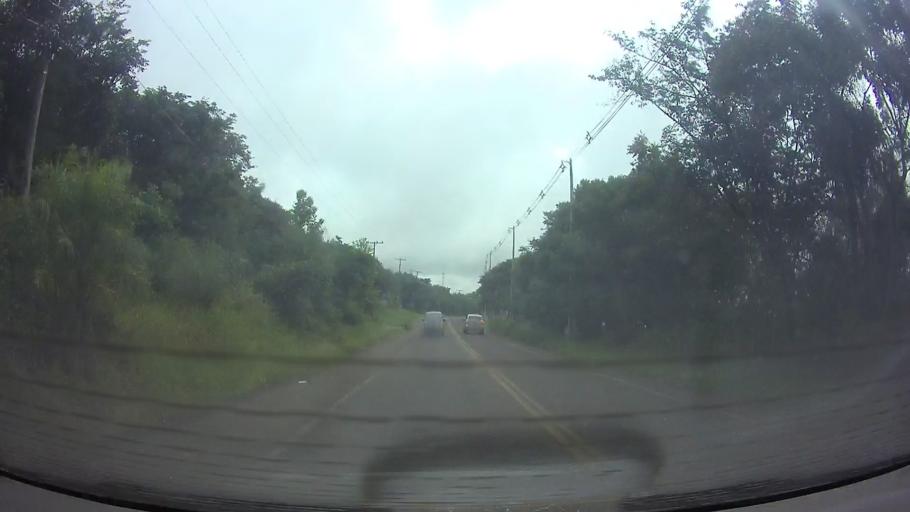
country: PY
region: Cordillera
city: Altos
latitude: -25.2850
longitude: -57.2626
